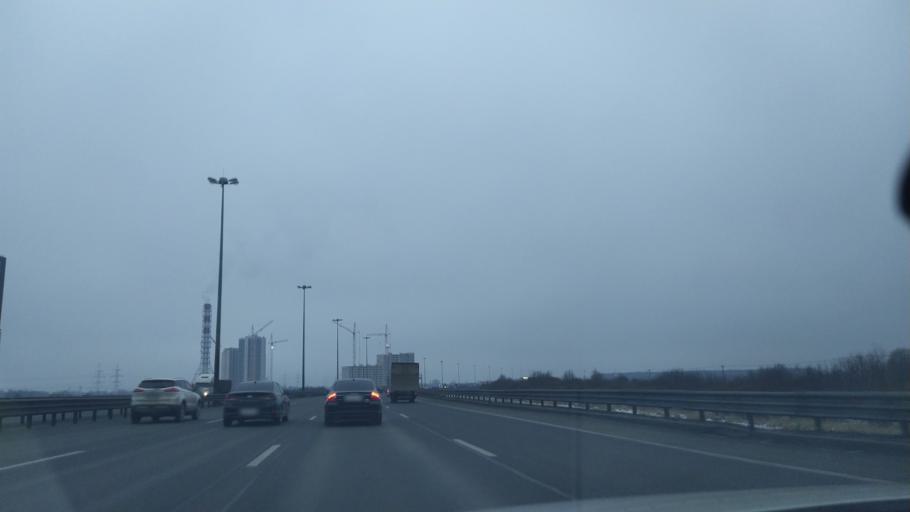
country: RU
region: St.-Petersburg
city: Krasnogvargeisky
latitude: 60.0105
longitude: 30.4742
